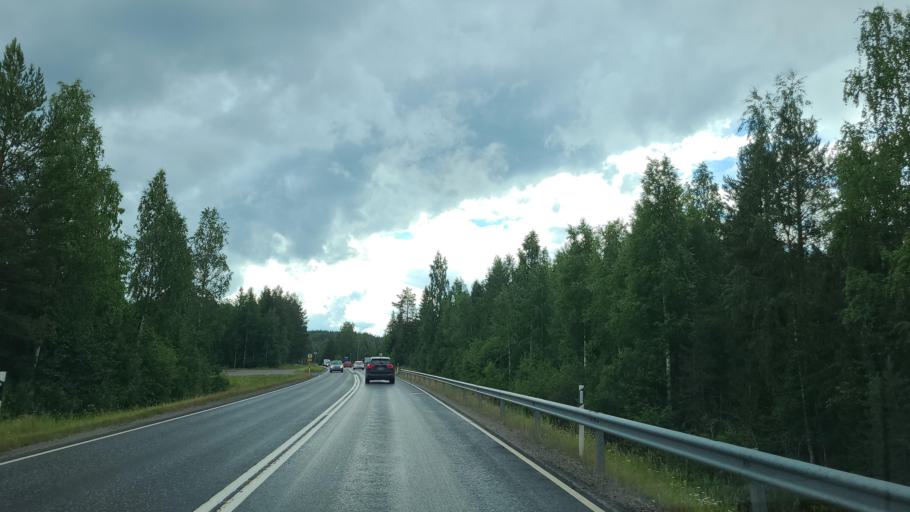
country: FI
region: Northern Savo
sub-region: Sisae-Savo
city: Rautalampi
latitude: 62.4819
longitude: 26.8699
